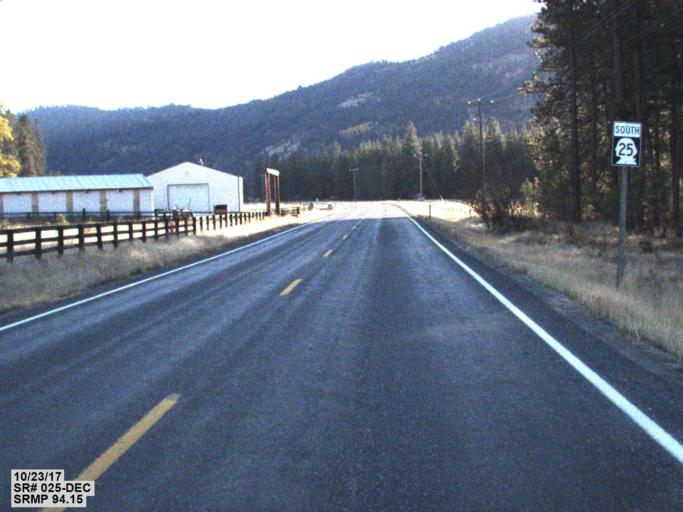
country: US
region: Washington
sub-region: Stevens County
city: Kettle Falls
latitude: 48.7494
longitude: -118.0464
